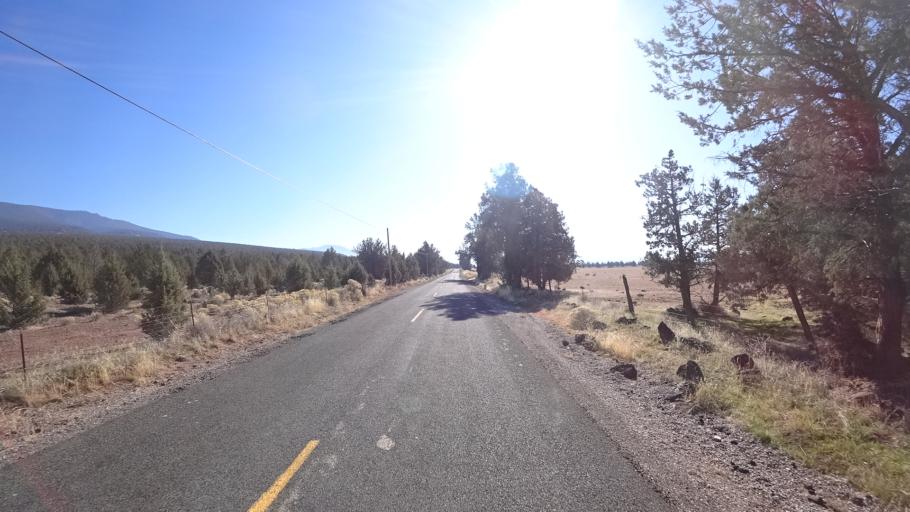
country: US
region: California
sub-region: Siskiyou County
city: Montague
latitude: 41.6340
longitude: -122.3374
